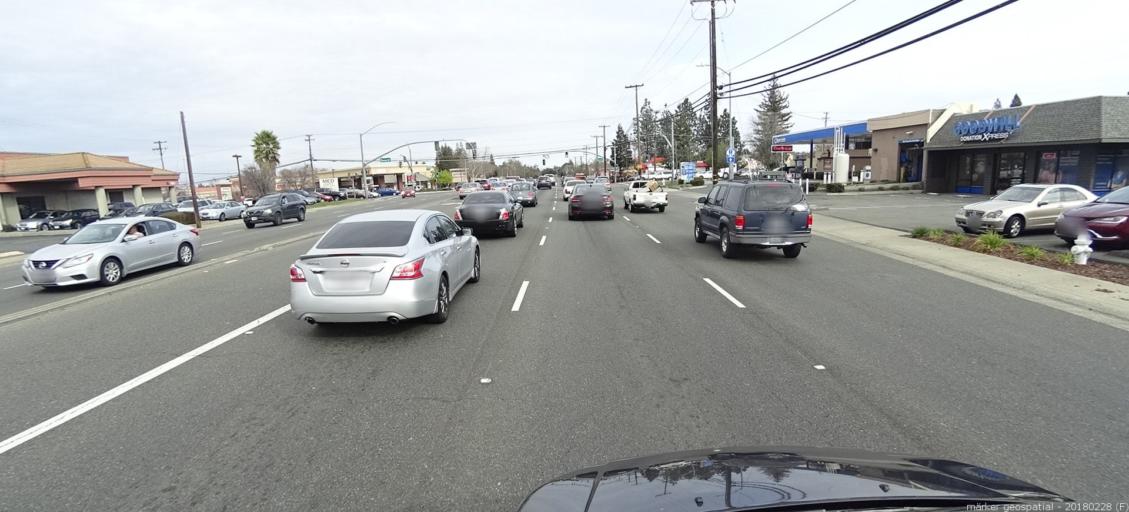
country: US
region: California
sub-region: Sacramento County
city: Fair Oaks
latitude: 38.6635
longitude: -121.3097
